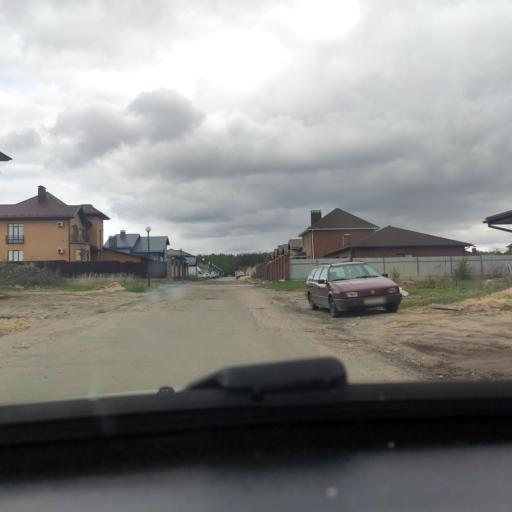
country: RU
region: Voronezj
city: Podgornoye
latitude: 51.7554
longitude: 39.1444
